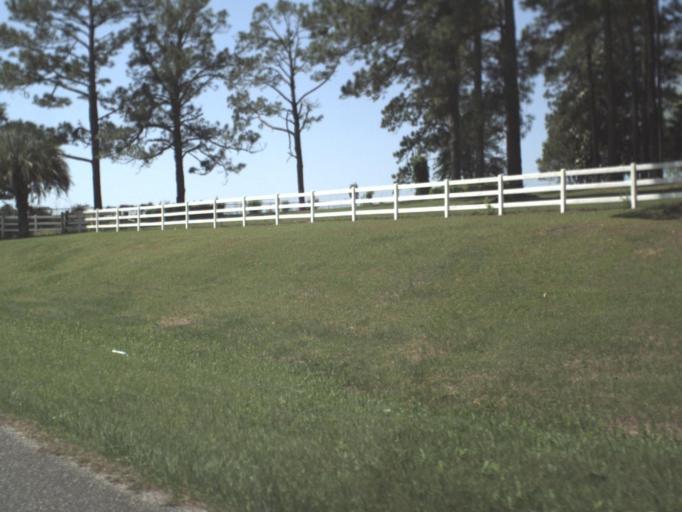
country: US
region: Florida
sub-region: Jefferson County
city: Monticello
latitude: 30.5714
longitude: -83.8701
